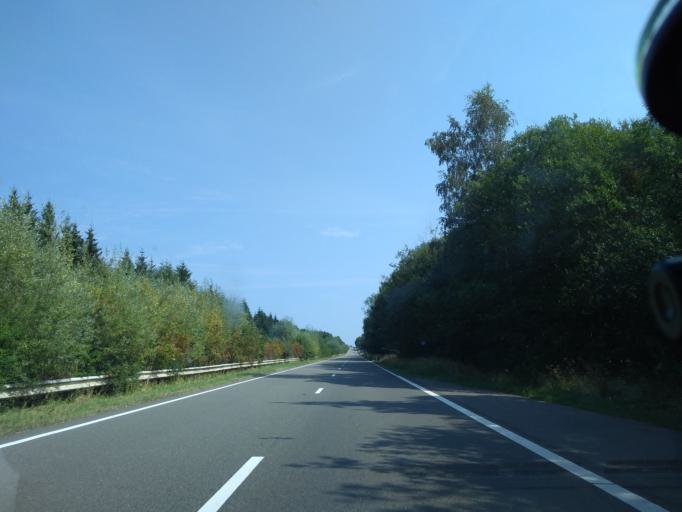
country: BE
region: Wallonia
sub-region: Province du Luxembourg
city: Tenneville
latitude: 50.0861
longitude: 5.4449
